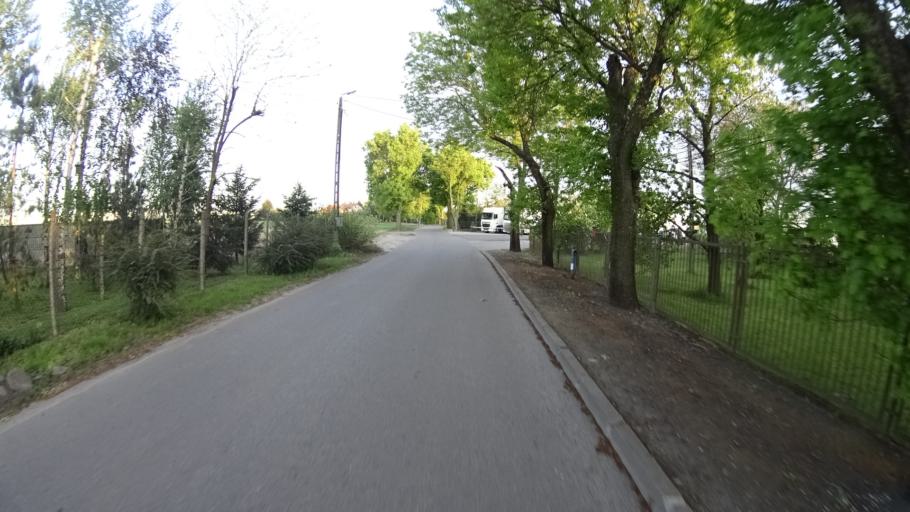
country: PL
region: Masovian Voivodeship
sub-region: Powiat warszawski zachodni
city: Ozarow Mazowiecki
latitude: 52.2061
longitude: 20.7561
